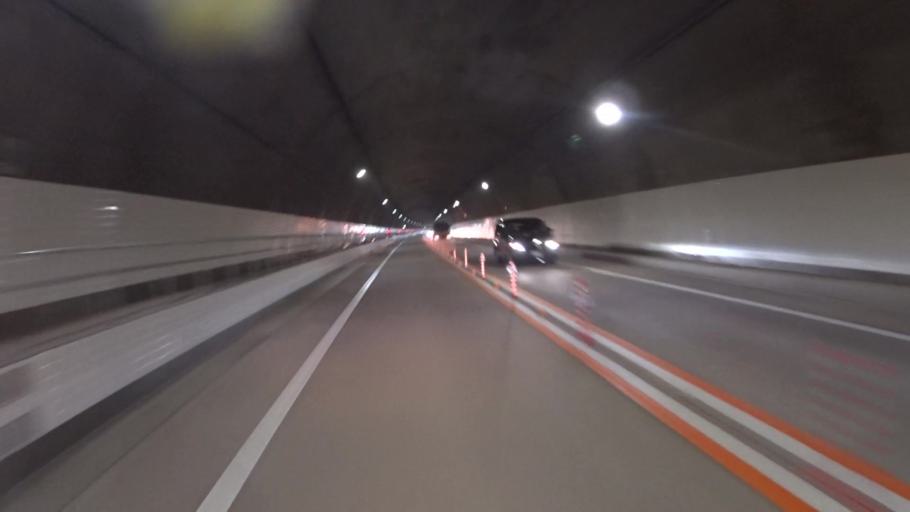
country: JP
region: Kyoto
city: Ayabe
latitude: 35.2373
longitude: 135.3437
